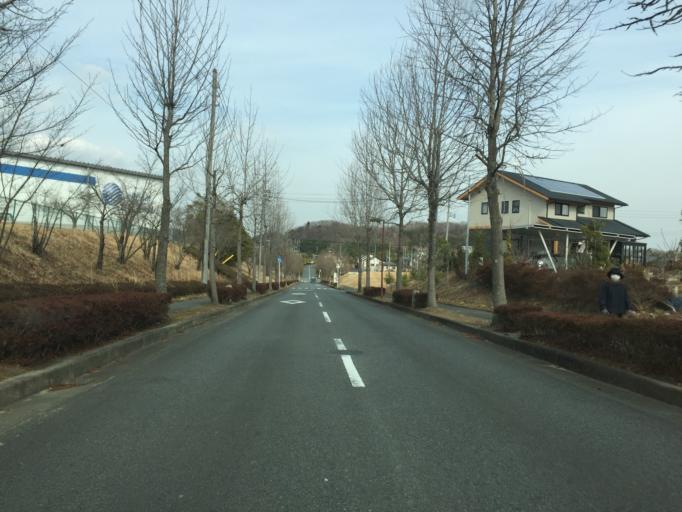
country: JP
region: Ibaraki
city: Kitaibaraki
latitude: 36.9331
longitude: 140.7451
